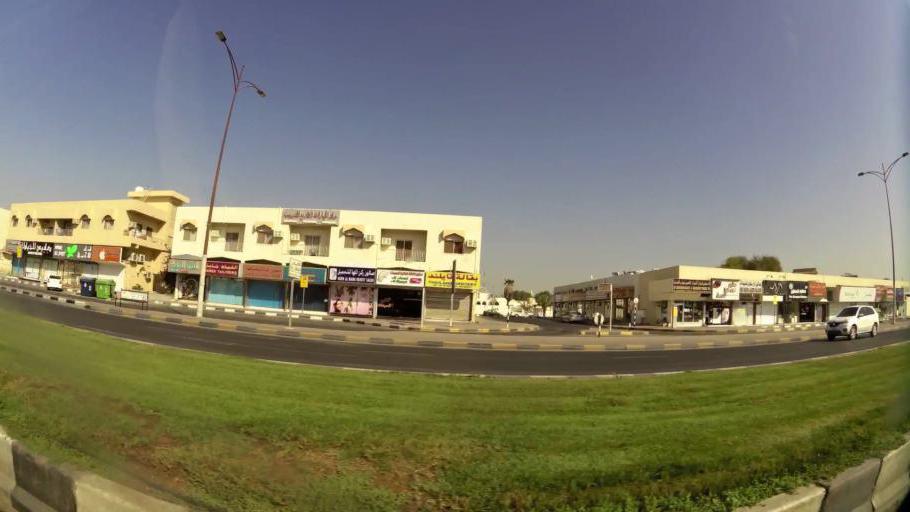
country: AE
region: Ash Shariqah
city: Sharjah
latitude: 25.3478
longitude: 55.4342
